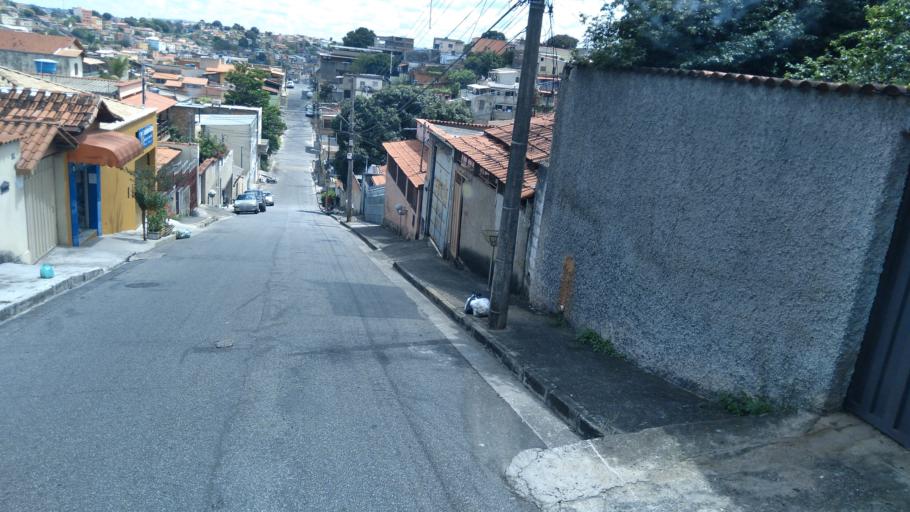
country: BR
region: Minas Gerais
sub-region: Belo Horizonte
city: Belo Horizonte
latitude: -19.8716
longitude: -43.9087
